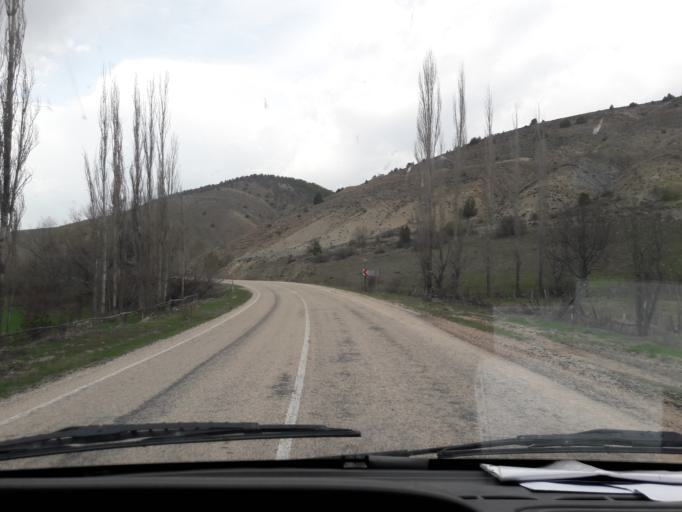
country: TR
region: Giresun
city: Alucra
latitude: 40.2871
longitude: 38.8196
